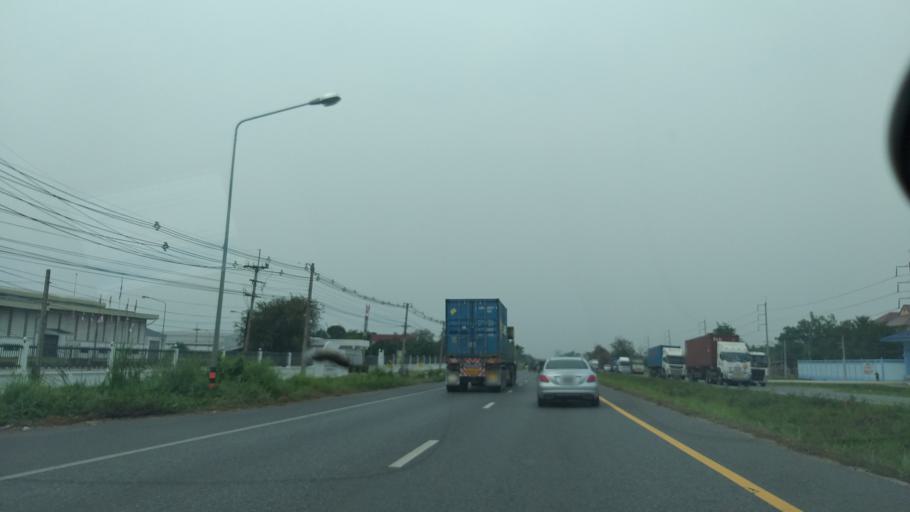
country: TH
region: Chon Buri
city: Ko Chan
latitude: 13.3634
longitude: 101.2737
